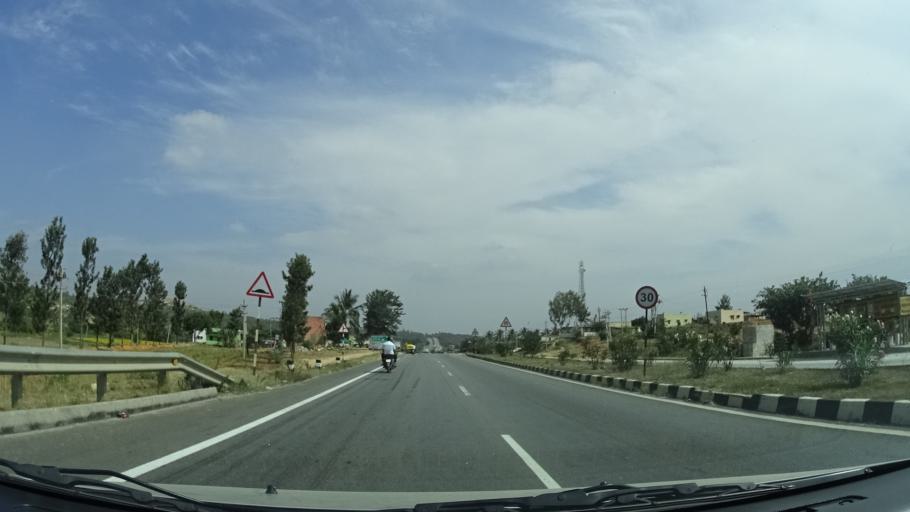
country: IN
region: Karnataka
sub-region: Chikkaballapur
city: Chik Ballapur
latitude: 13.5388
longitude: 77.7690
